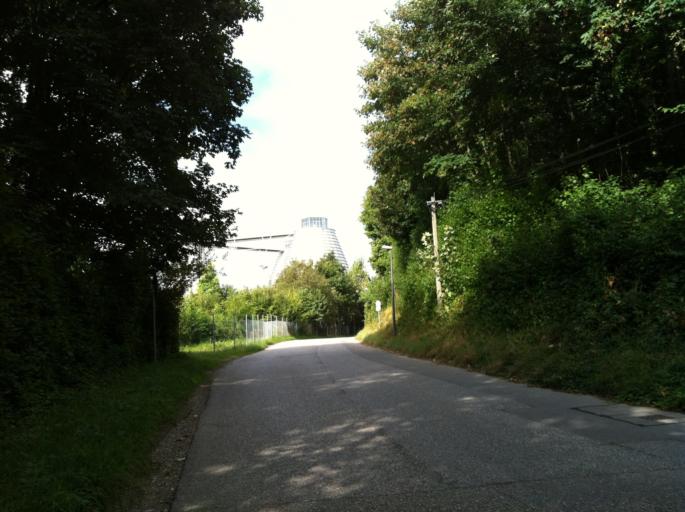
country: DE
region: Bavaria
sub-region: Upper Bavaria
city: Unterfoehring
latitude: 48.2121
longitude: 11.6293
